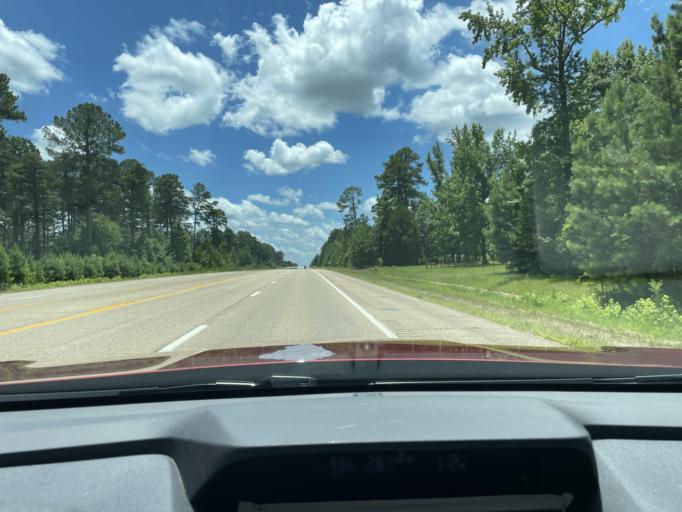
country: US
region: Arkansas
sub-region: Drew County
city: Monticello
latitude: 33.6927
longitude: -91.8064
